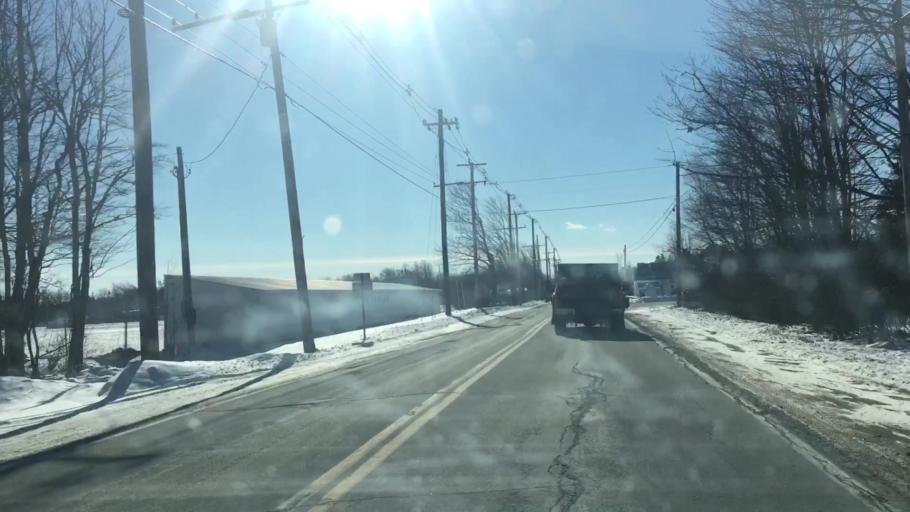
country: US
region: Maine
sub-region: Hancock County
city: Surry
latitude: 44.4319
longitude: -68.5746
